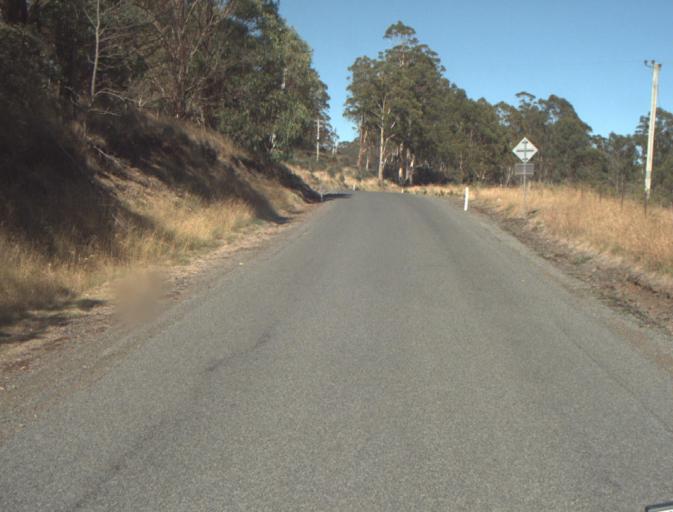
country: AU
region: Tasmania
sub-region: Launceston
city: Newstead
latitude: -41.3667
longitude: 147.3038
